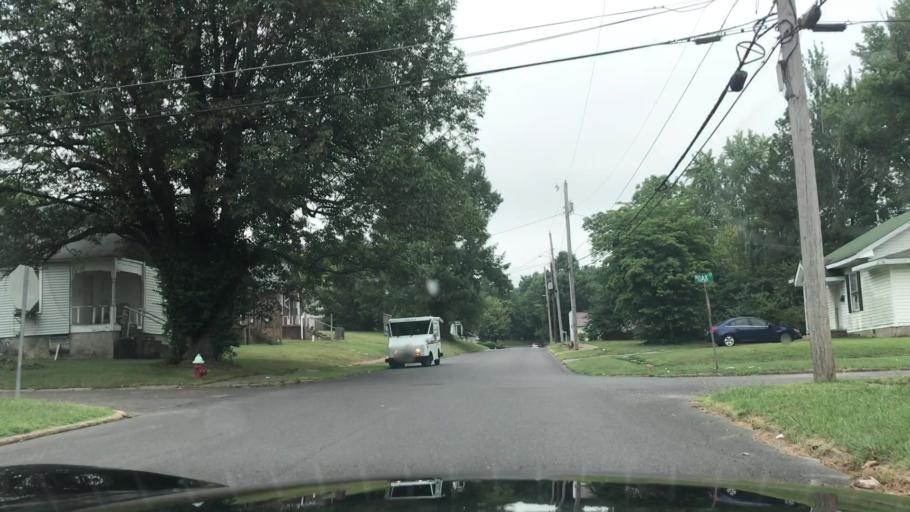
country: US
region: Kentucky
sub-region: Graves County
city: Mayfield
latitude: 36.7361
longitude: -88.6410
